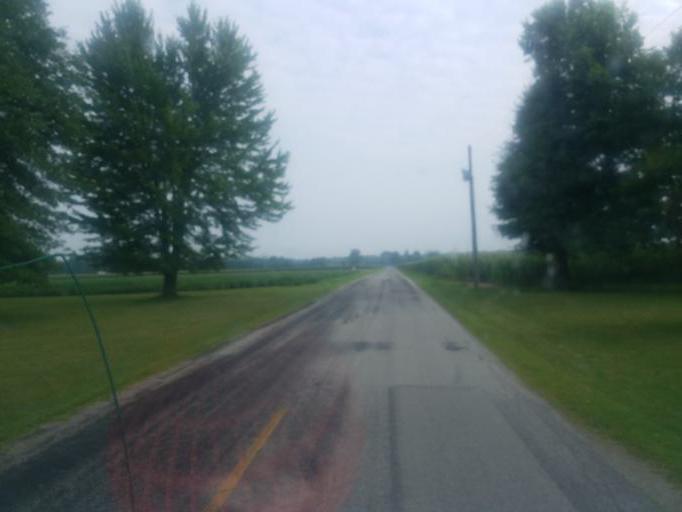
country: US
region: Ohio
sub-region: Morrow County
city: Cardington
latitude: 40.5800
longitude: -82.9766
